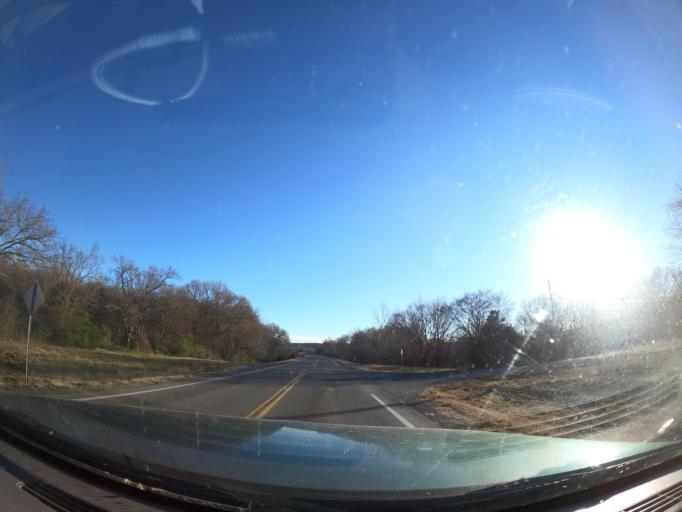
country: US
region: Oklahoma
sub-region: Latimer County
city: Wilburton
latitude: 34.9398
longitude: -95.3412
